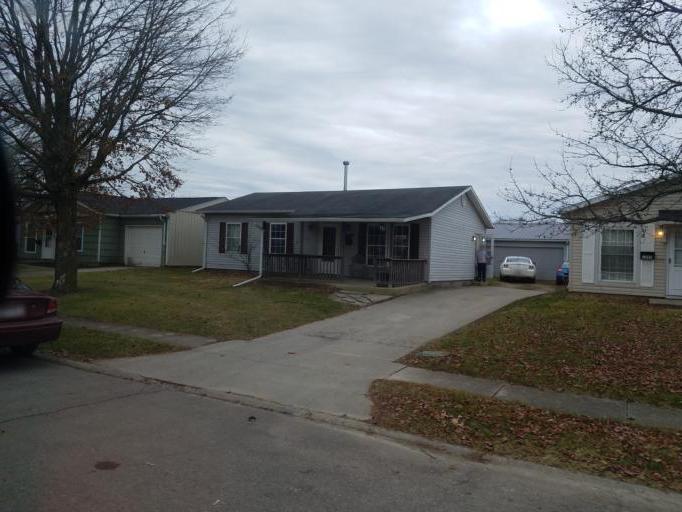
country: US
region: Ohio
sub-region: Marion County
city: Marion
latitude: 40.6099
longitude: -83.1159
